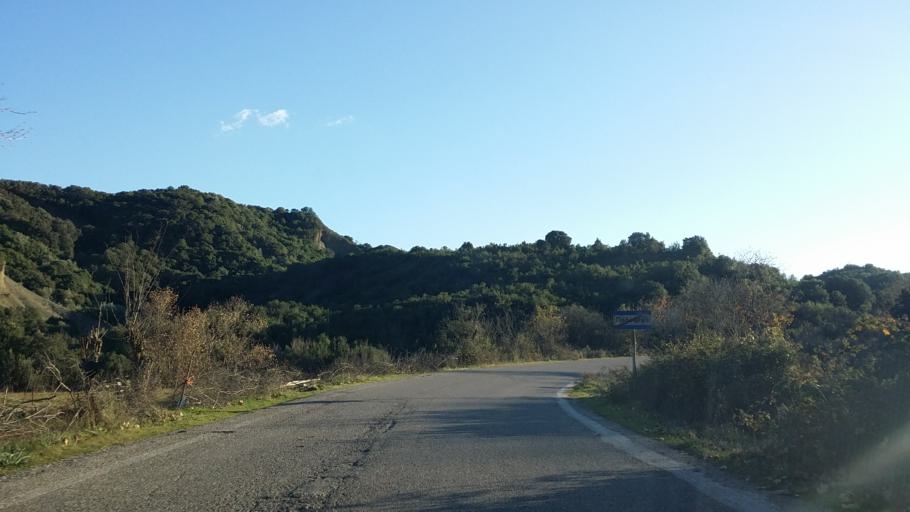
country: GR
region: West Greece
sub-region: Nomos Aitolias kai Akarnanias
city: Sardinia
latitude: 38.8501
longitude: 21.3342
